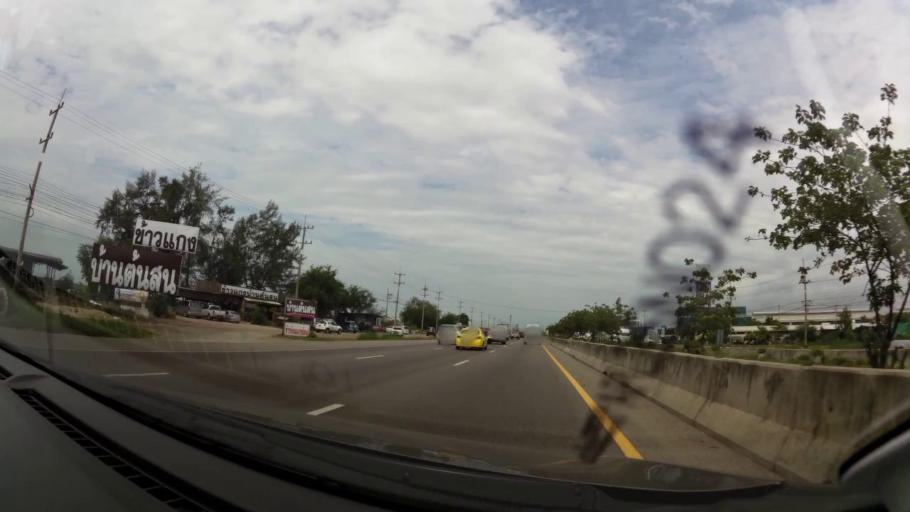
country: TH
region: Samut Songkhram
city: Samut Songkhram
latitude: 13.4565
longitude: 100.0909
